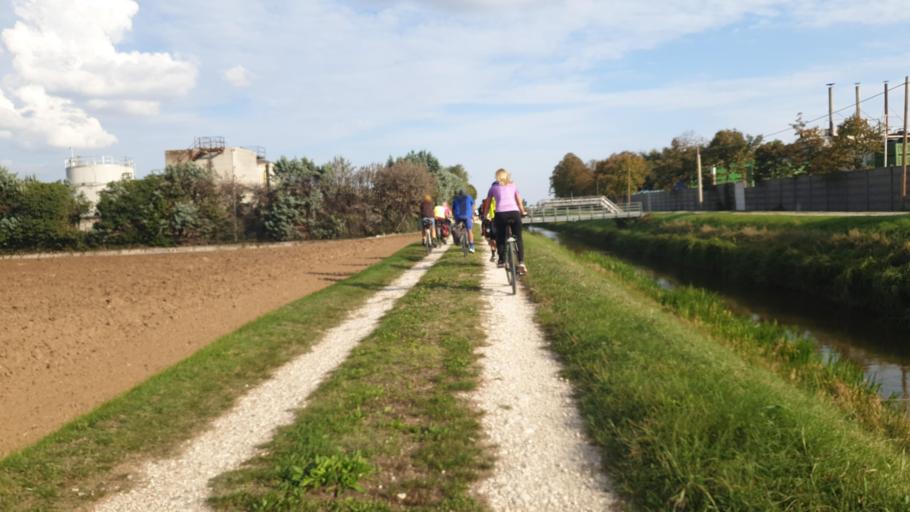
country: IT
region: Veneto
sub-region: Provincia di Vicenza
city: Poiana Maggiore
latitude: 45.2740
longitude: 11.4864
